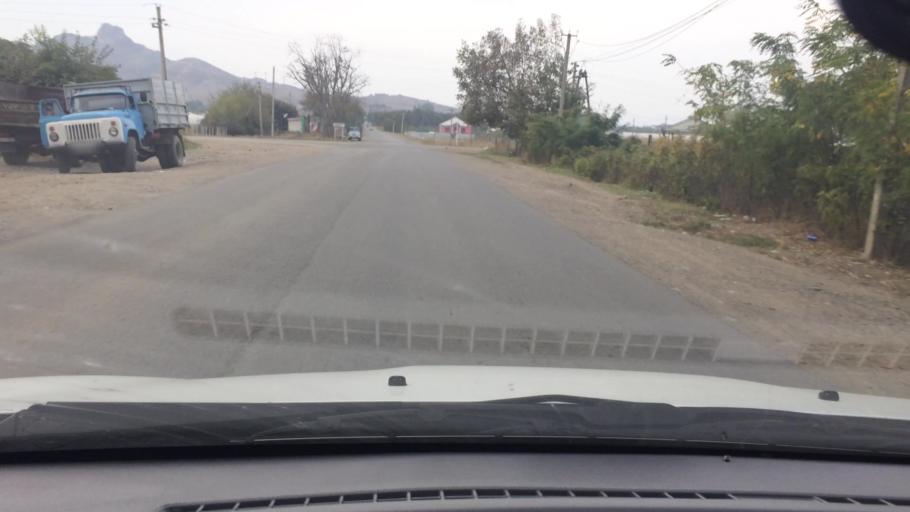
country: GE
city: Naghvarevi
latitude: 41.3547
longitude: 44.8588
